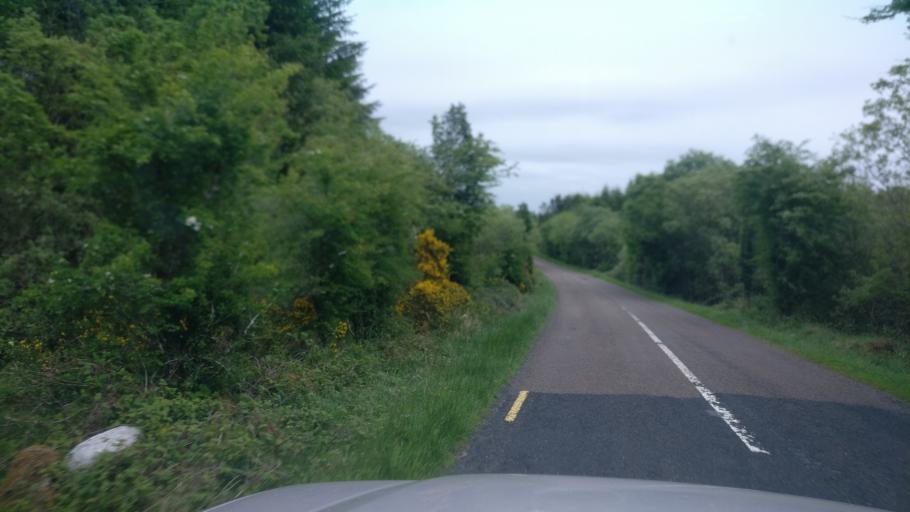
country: IE
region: Connaught
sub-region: County Galway
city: Loughrea
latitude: 53.0775
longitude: -8.5453
